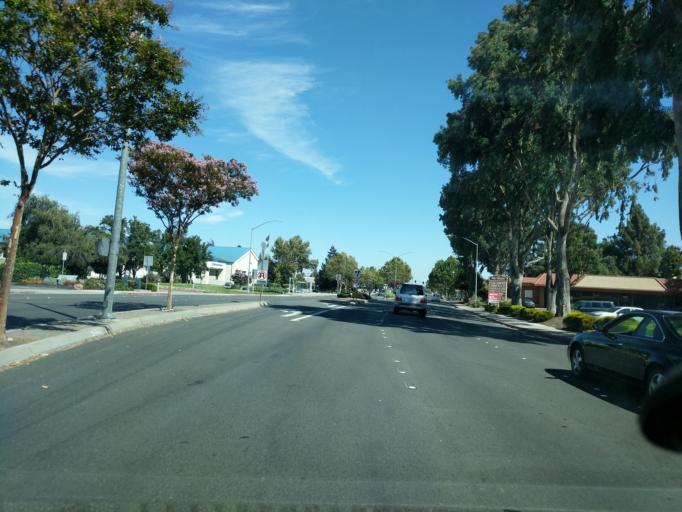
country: US
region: California
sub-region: Alameda County
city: Dublin
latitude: 37.7059
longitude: -121.9226
